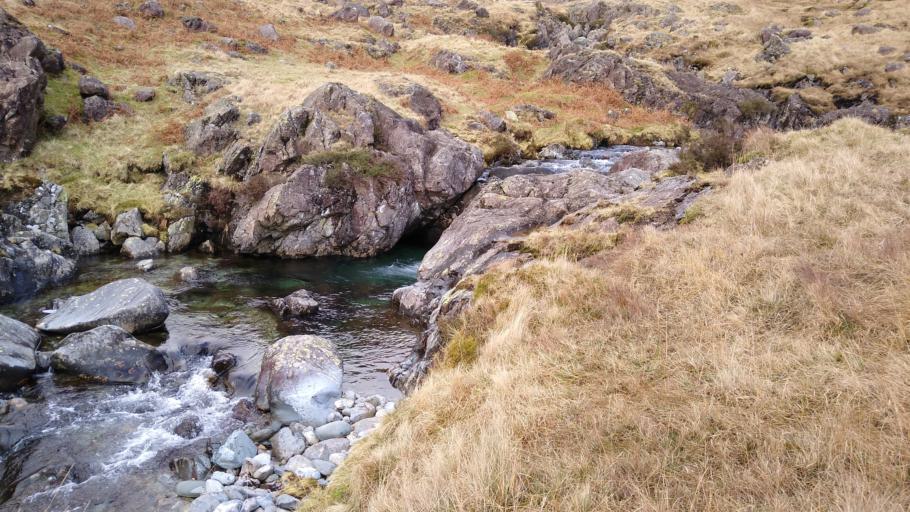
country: GB
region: England
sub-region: Cumbria
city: Keswick
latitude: 54.4263
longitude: -3.1890
